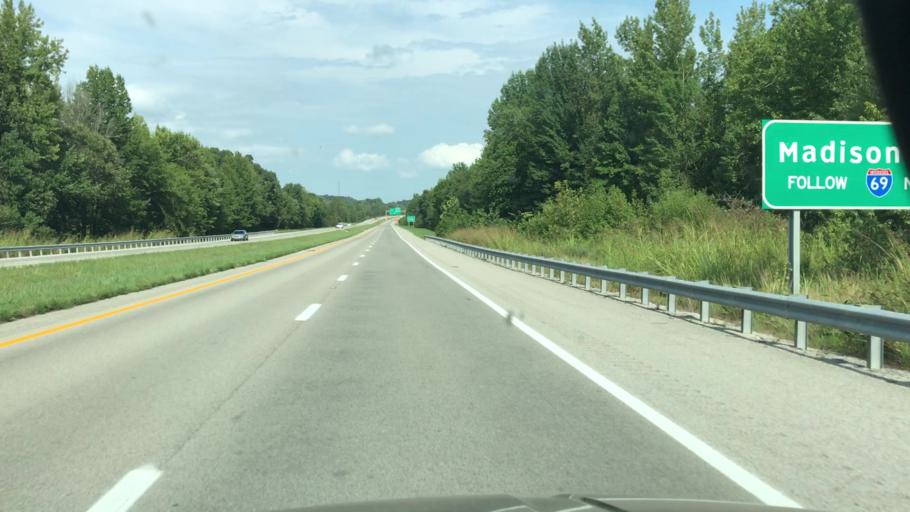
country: US
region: Kentucky
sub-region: Hopkins County
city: Nortonville
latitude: 37.2106
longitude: -87.4808
